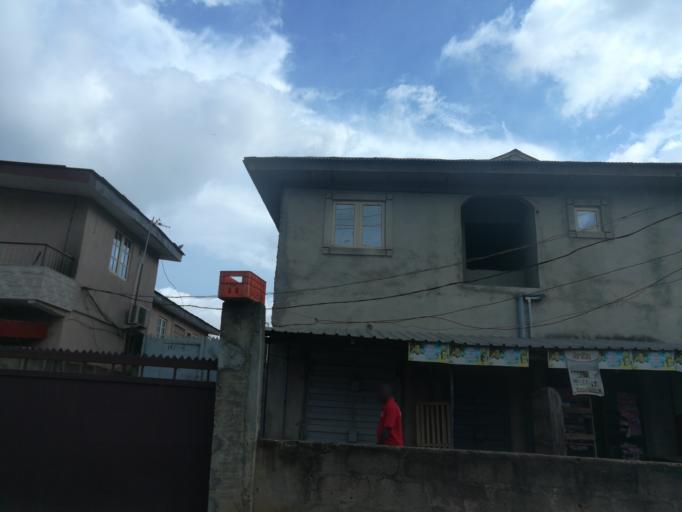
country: NG
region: Lagos
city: Somolu
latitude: 6.5464
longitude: 3.3749
